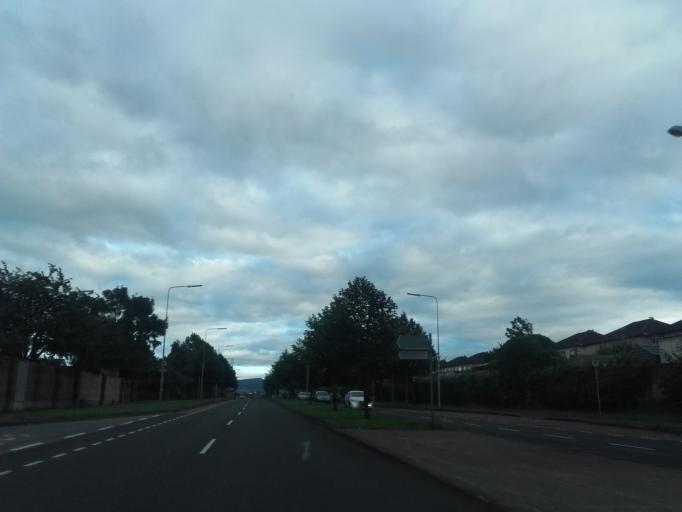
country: IE
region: Leinster
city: Tallaght
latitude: 53.3028
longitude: -6.3770
